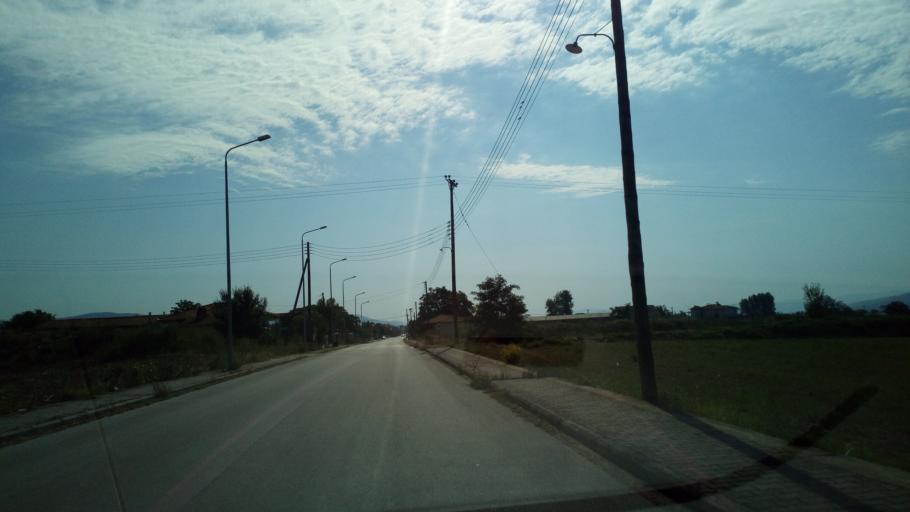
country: GR
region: Central Macedonia
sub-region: Nomos Thessalonikis
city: Askos
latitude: 40.6929
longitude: 23.3216
